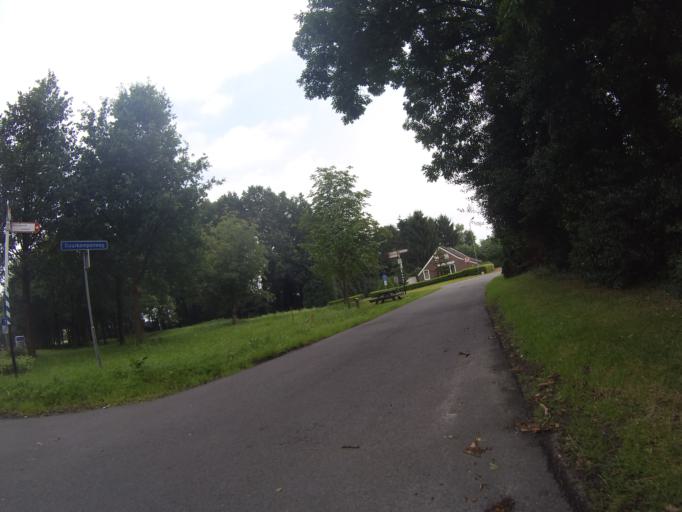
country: NL
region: Drenthe
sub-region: Gemeente Emmen
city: Emmen
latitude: 52.8253
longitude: 6.9165
